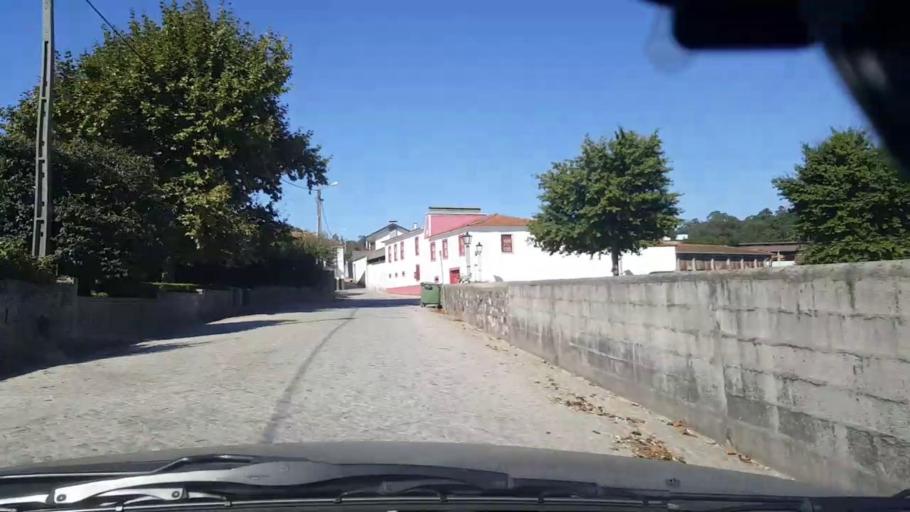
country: PT
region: Braga
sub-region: Vila Nova de Famalicao
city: Ribeirao
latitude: 41.3607
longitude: -8.6367
